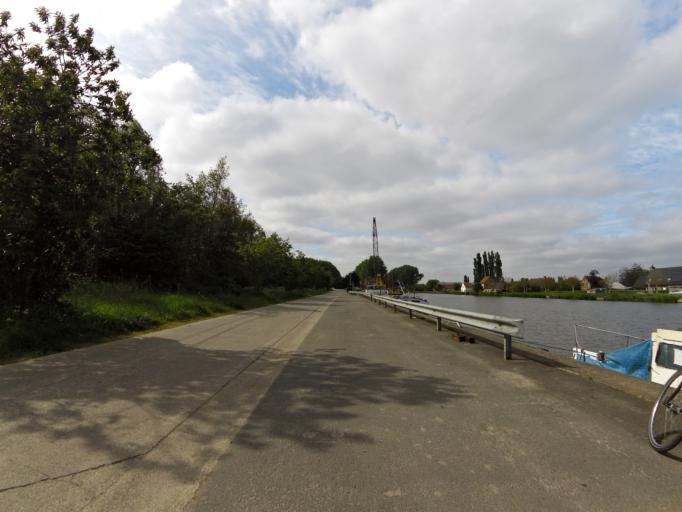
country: BE
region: Flanders
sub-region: Provincie West-Vlaanderen
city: Oostkamp
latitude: 51.1602
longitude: 3.2593
